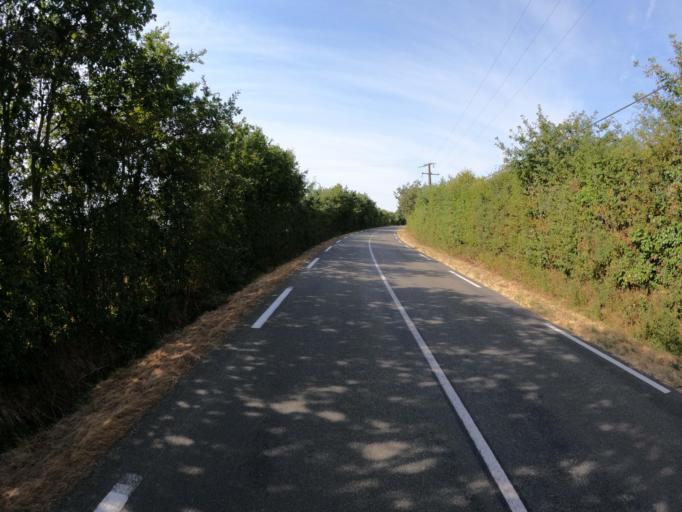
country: FR
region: Pays de la Loire
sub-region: Departement de la Vendee
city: Falleron
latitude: 46.8661
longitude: -1.7072
